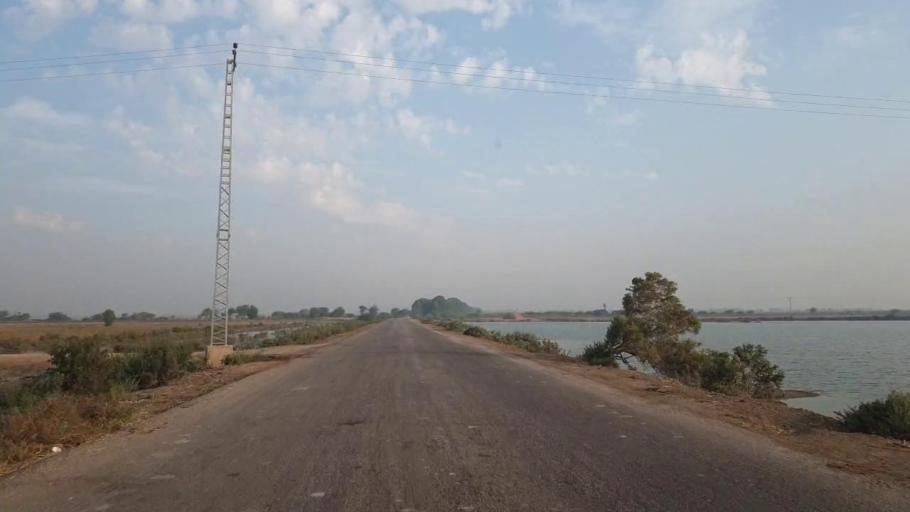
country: PK
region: Sindh
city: Tando Bago
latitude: 24.7229
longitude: 68.9423
